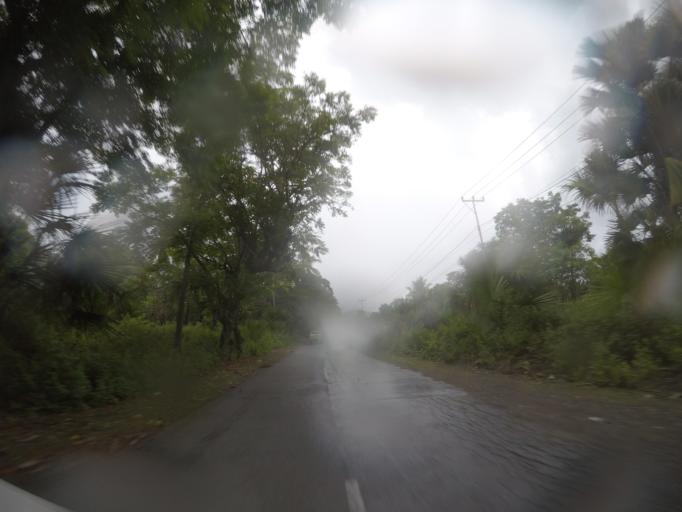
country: ID
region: East Nusa Tenggara
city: Atambua
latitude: -8.9579
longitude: 124.9852
